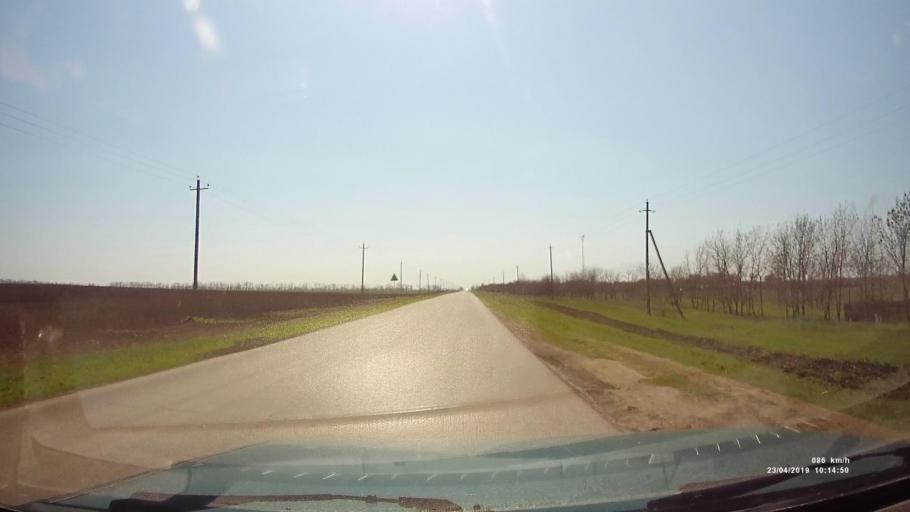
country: RU
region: Rostov
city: Sovetskoye
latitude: 46.6732
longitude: 42.3749
